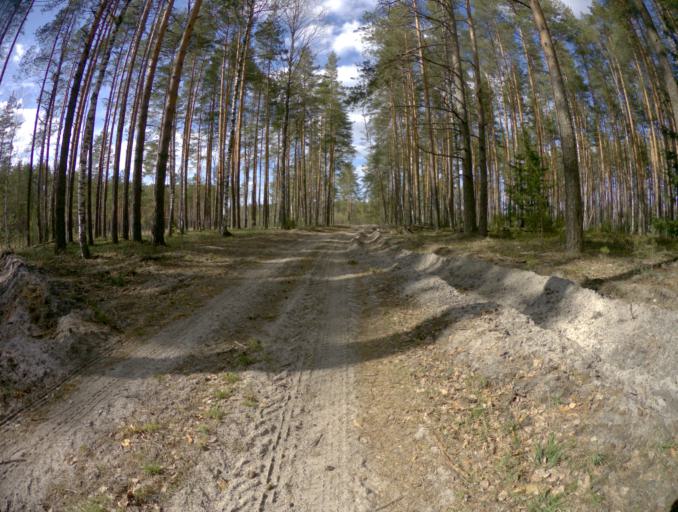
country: RU
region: Vladimir
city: Vorsha
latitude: 55.8845
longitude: 40.1754
